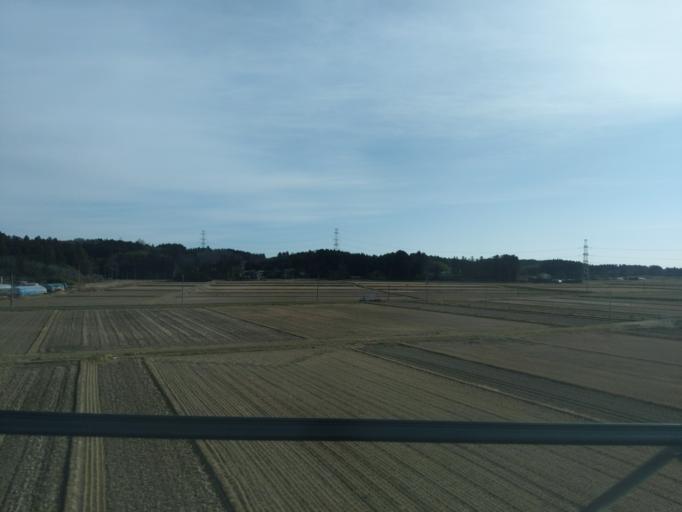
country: JP
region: Miyagi
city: Furukawa
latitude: 38.6251
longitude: 141.0003
